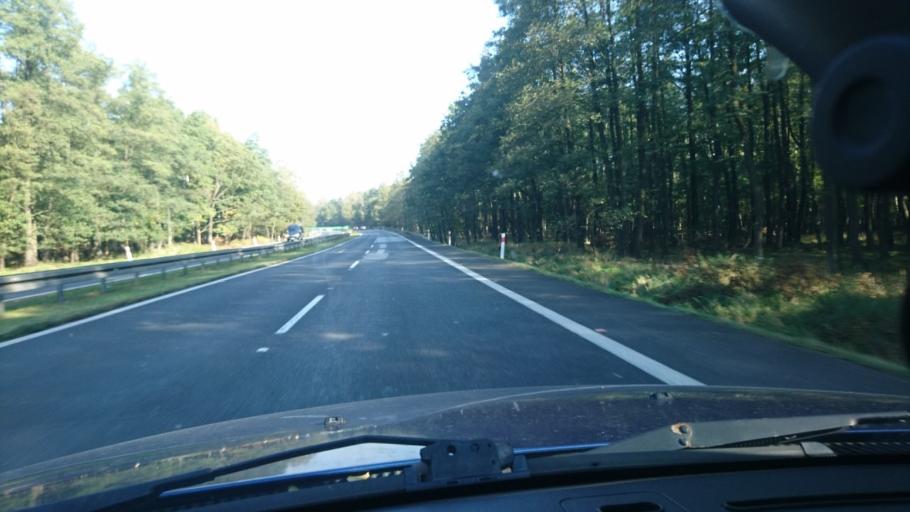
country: PL
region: Silesian Voivodeship
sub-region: Katowice
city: Murcki
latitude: 50.1496
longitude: 19.0238
